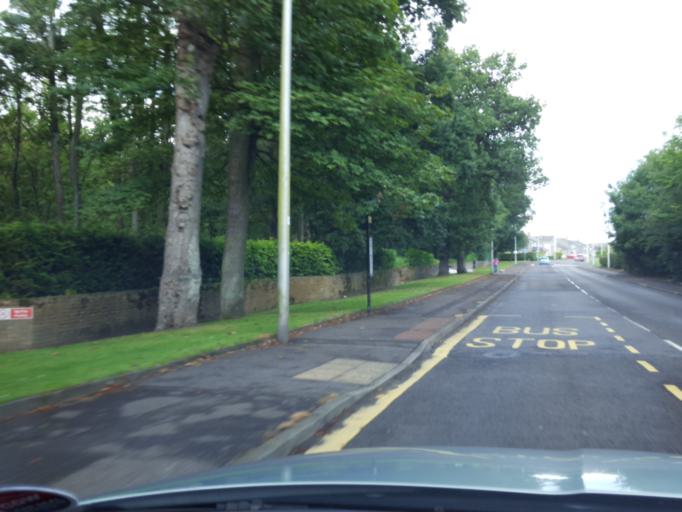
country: GB
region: Scotland
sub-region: Fife
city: Inverkeithing
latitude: 56.0549
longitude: -3.4143
